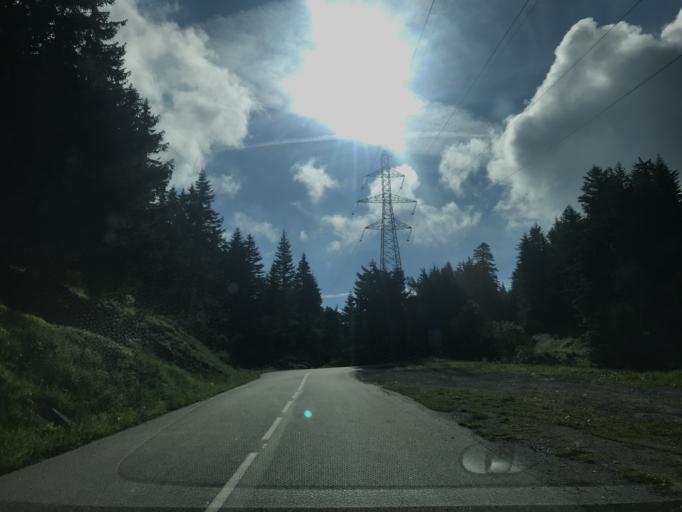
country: FR
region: Rhone-Alpes
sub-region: Departement de la Savoie
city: Modane
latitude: 45.2107
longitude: 6.6408
